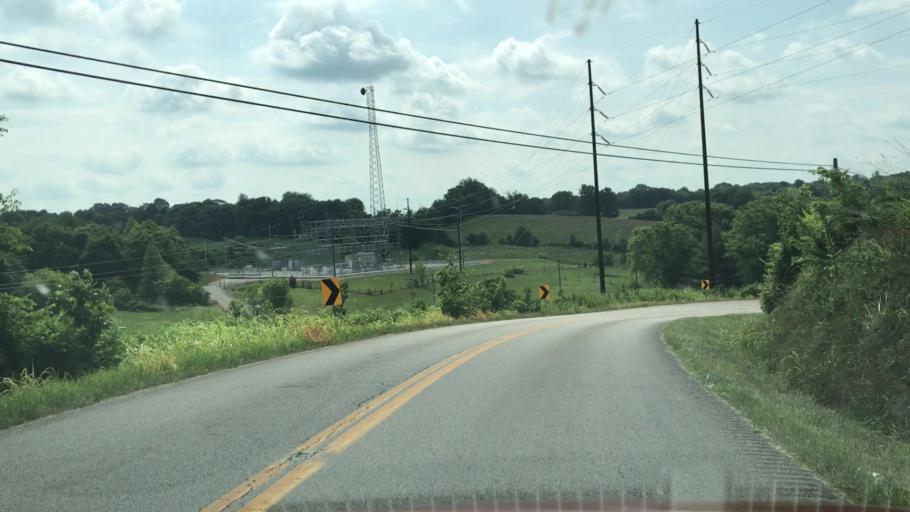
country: US
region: Kentucky
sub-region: Barren County
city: Glasgow
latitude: 36.9721
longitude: -85.8943
